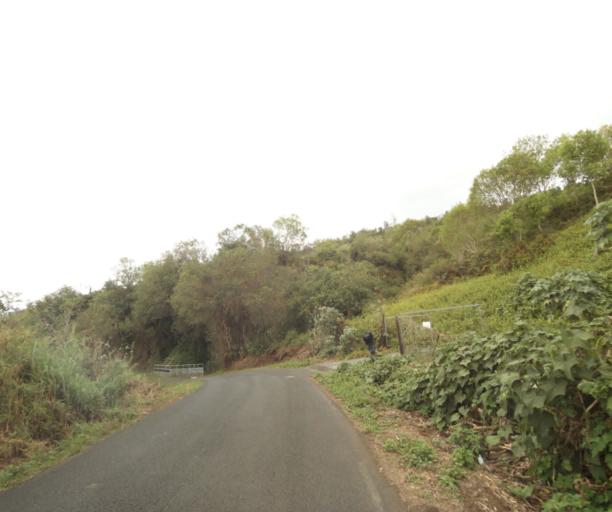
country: RE
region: Reunion
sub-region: Reunion
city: Saint-Paul
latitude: -21.0107
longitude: 55.3414
